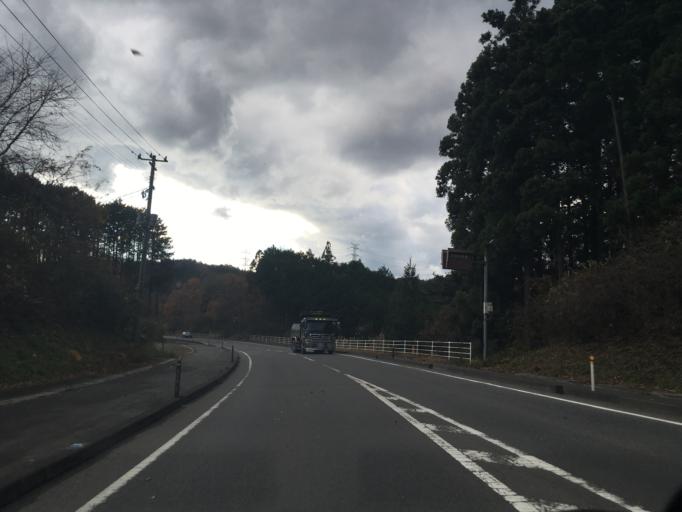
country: JP
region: Fukushima
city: Ishikawa
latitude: 37.0430
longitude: 140.3746
